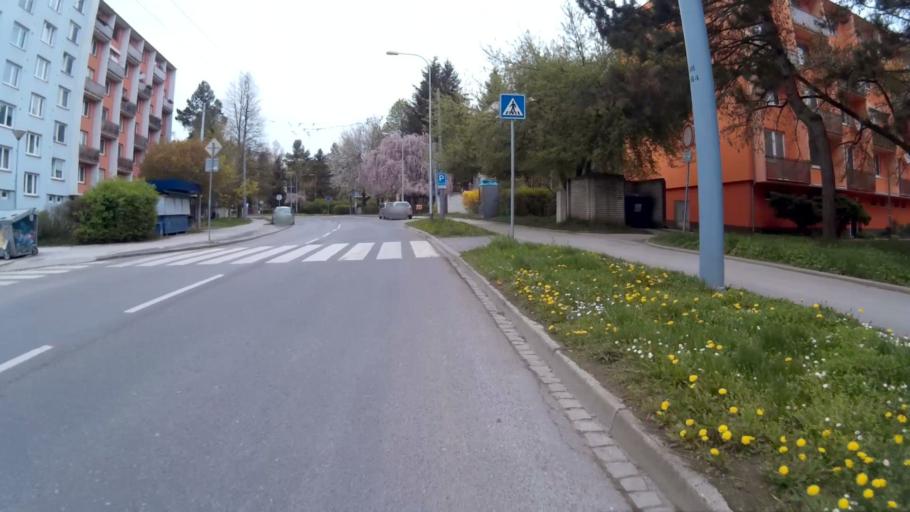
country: CZ
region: South Moravian
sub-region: Mesto Brno
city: Mokra Hora
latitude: 49.2245
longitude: 16.5583
